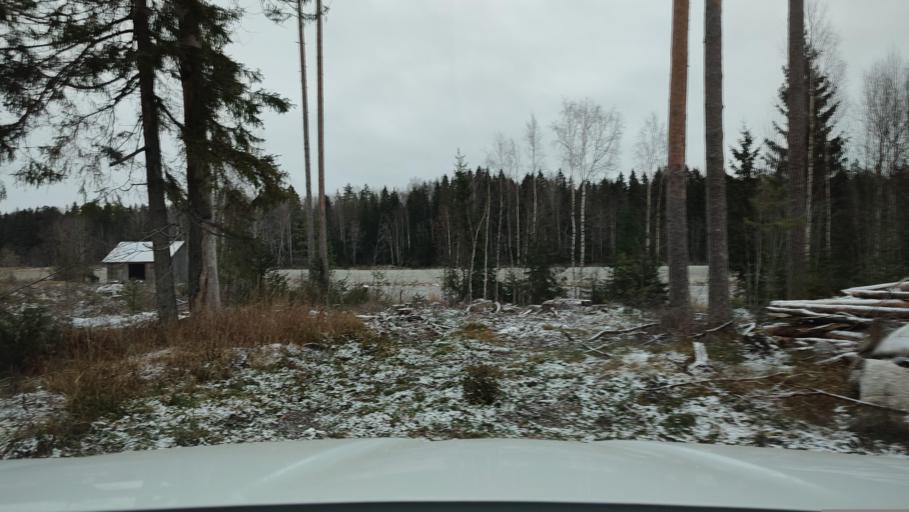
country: FI
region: Ostrobothnia
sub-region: Vaasa
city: Ristinummi
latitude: 62.9393
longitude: 21.7582
